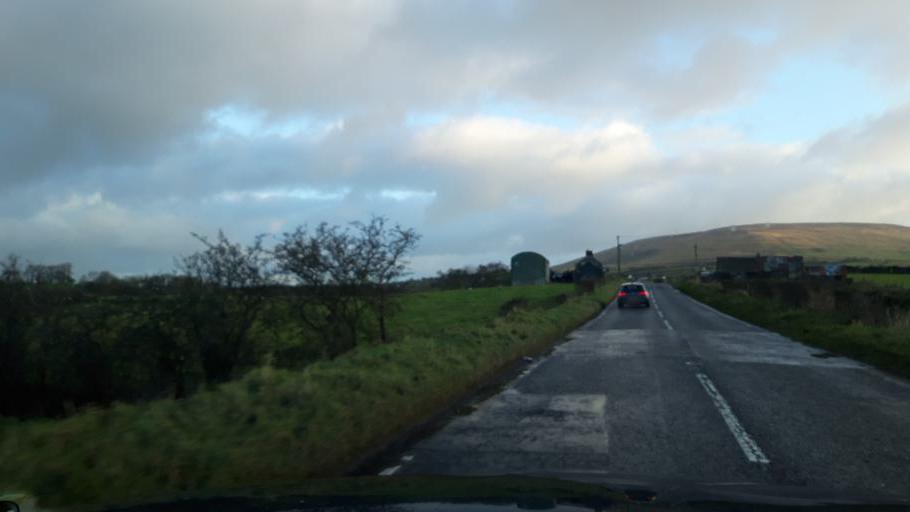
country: GB
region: Northern Ireland
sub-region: Moyle District
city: Ballycastle
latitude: 55.1451
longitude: -6.3154
